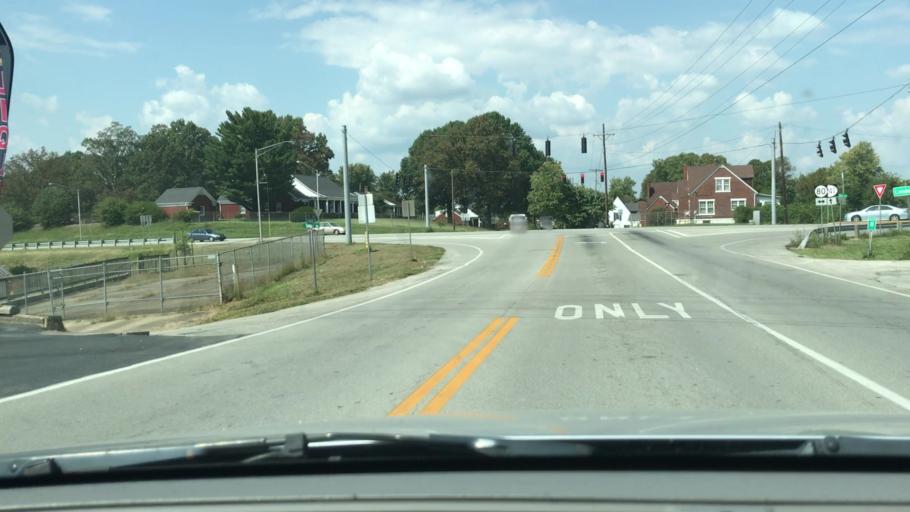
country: US
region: Kentucky
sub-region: Pulaski County
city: Somerset
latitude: 37.1006
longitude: -84.6083
